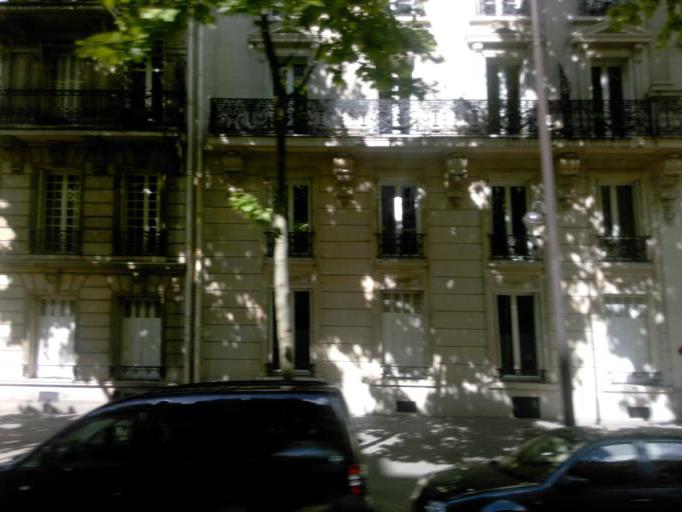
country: FR
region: Ile-de-France
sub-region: Departement des Hauts-de-Seine
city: Clichy
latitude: 48.8864
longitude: 2.3058
